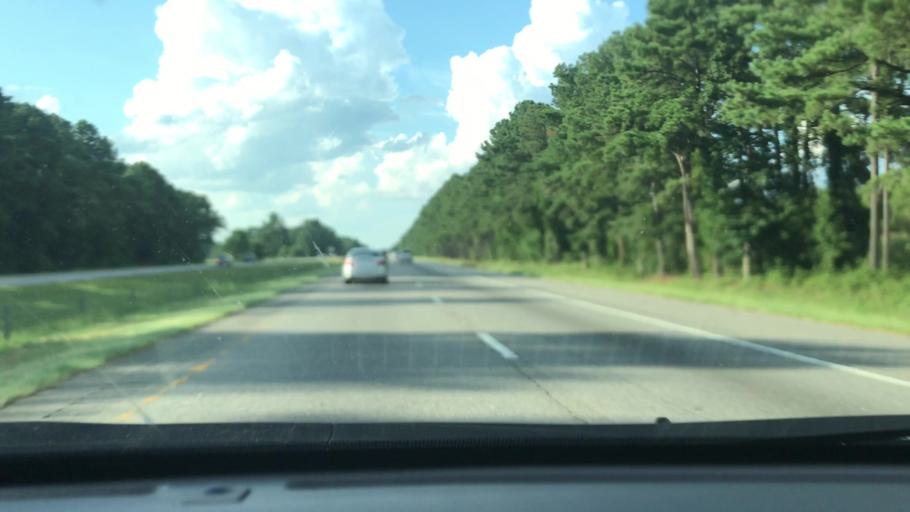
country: US
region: North Carolina
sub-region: Robeson County
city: Saint Pauls
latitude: 34.7619
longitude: -78.9968
